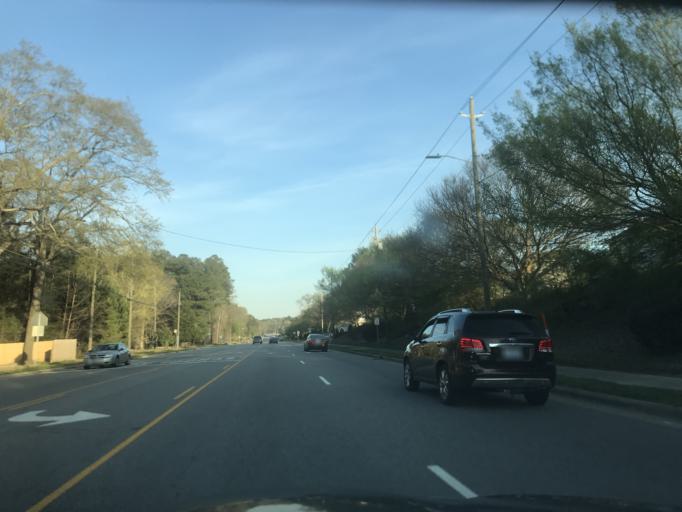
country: US
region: North Carolina
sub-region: Wake County
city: Garner
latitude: 35.7446
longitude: -78.5813
